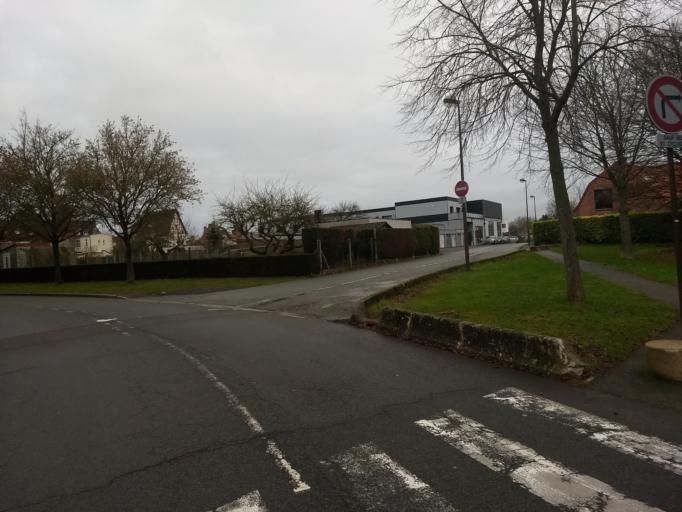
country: FR
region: Nord-Pas-de-Calais
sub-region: Departement du Pas-de-Calais
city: Achicourt
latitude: 50.2869
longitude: 2.7552
